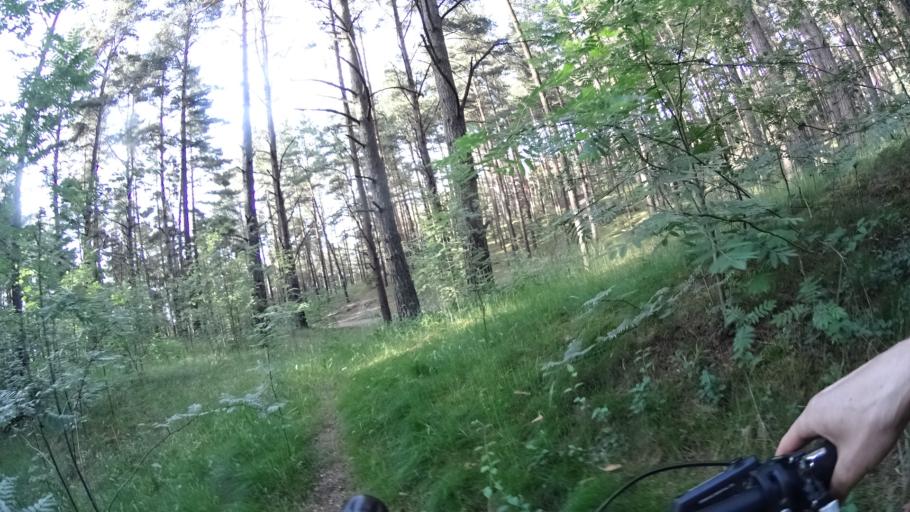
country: LV
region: Riga
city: Jaunciems
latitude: 57.0815
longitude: 24.1155
